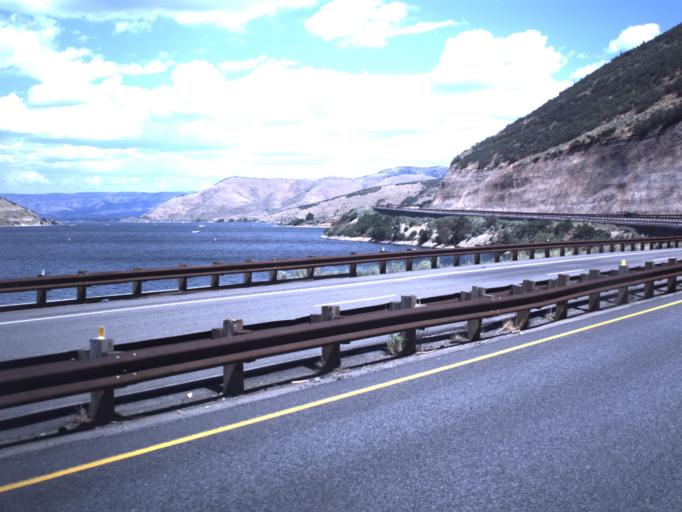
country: US
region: Utah
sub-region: Wasatch County
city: Midway
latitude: 40.4054
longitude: -111.5254
